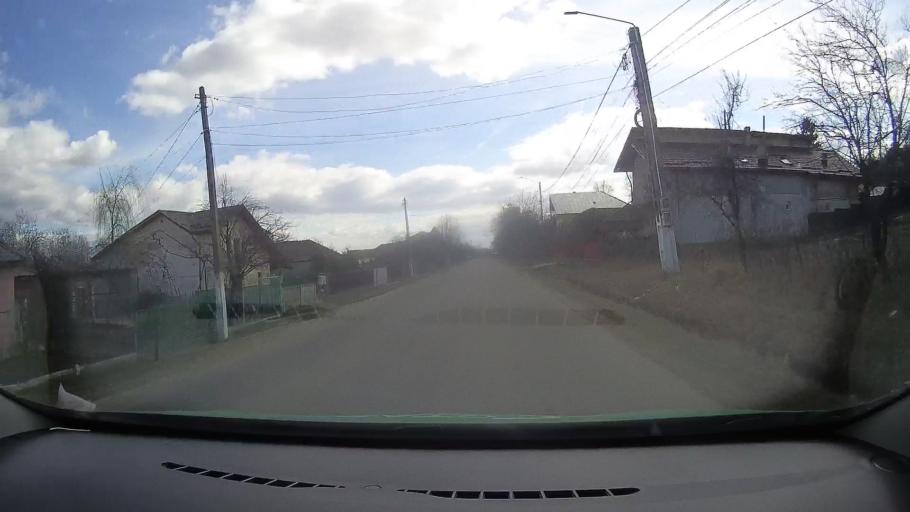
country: RO
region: Dambovita
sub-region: Comuna Sotanga
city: Teis
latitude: 44.9676
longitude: 25.3986
